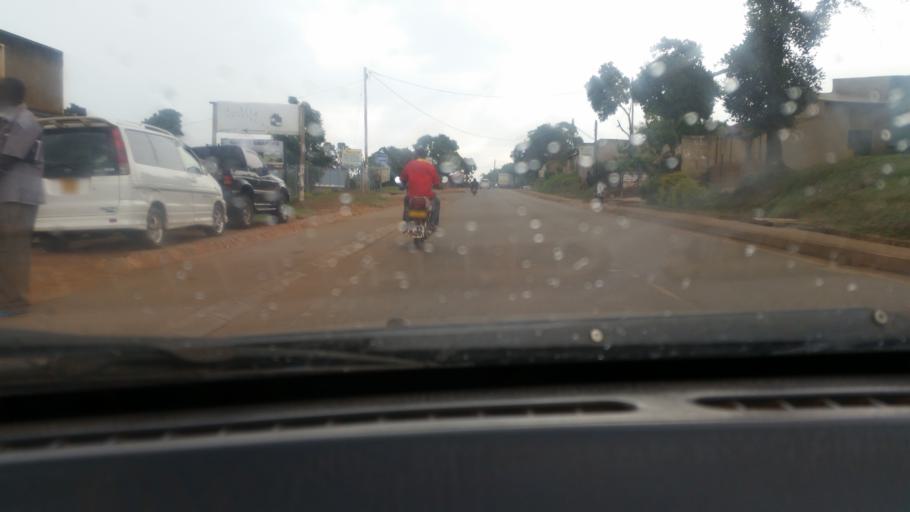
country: UG
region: Central Region
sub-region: Wakiso District
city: Kireka
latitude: 0.3521
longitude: 32.6509
